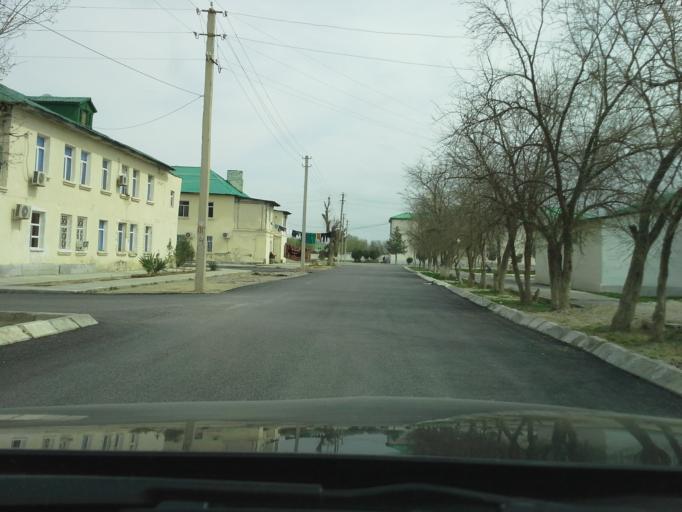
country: TM
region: Ahal
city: Abadan
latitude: 38.0616
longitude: 58.1536
